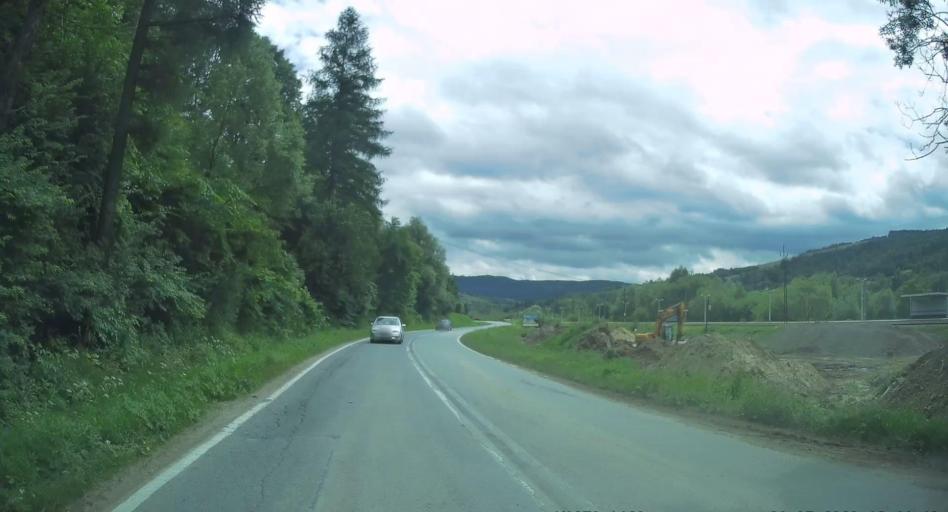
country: PL
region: Lesser Poland Voivodeship
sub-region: Powiat nowosadecki
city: Muszyna
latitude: 49.3415
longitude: 20.8212
